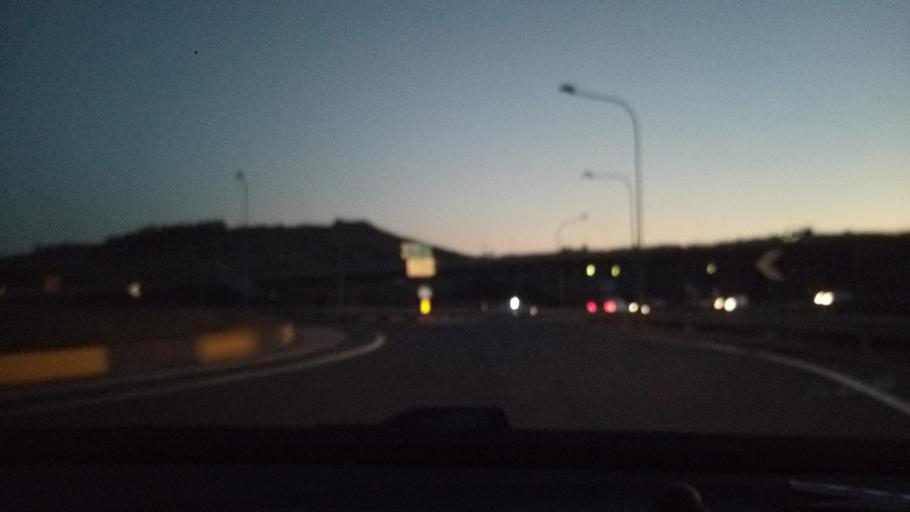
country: IT
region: Calabria
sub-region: Provincia di Catanzaro
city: Barone
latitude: 38.8631
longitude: 16.6333
